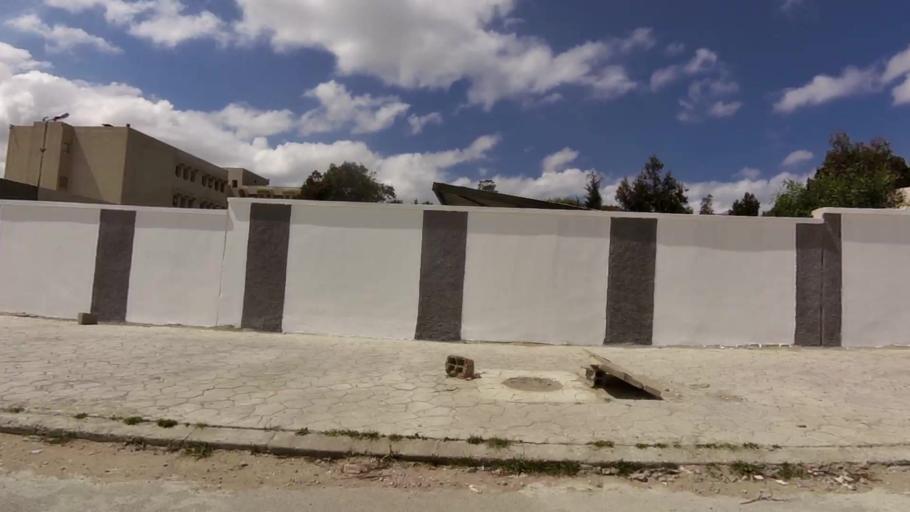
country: MA
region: Tanger-Tetouan
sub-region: Tanger-Assilah
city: Tangier
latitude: 35.7754
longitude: -5.7693
